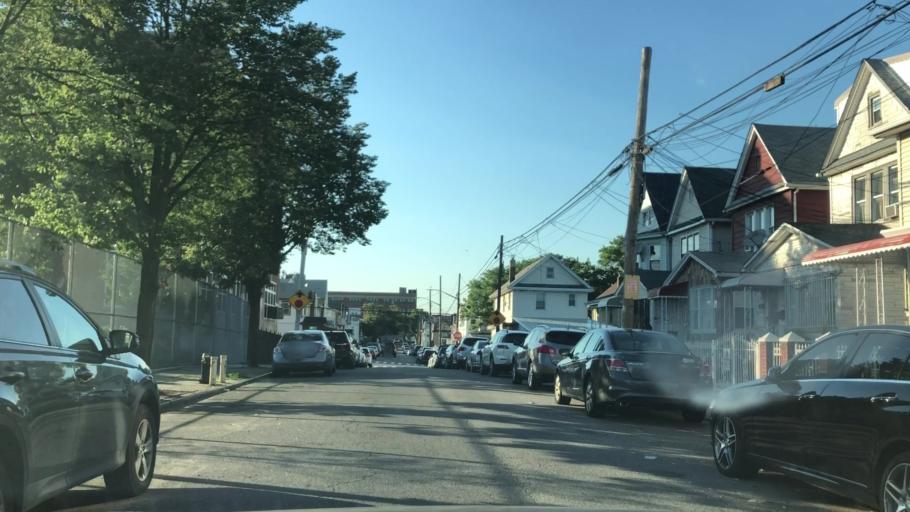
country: US
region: New York
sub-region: Queens County
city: Jamaica
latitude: 40.6935
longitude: -73.8156
